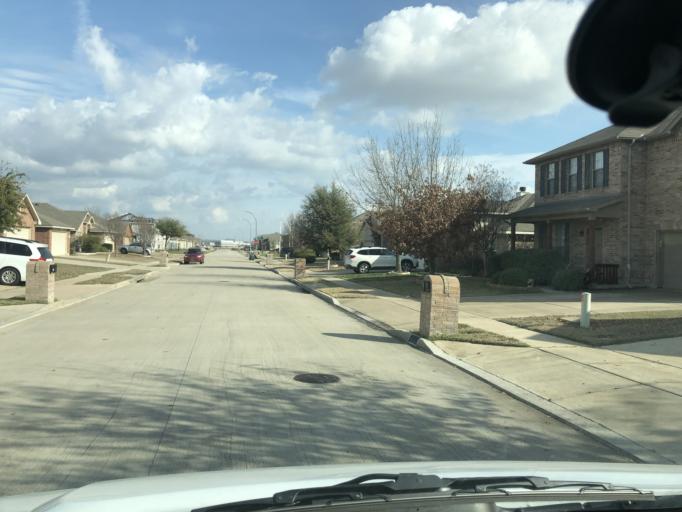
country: US
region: Texas
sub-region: Tarrant County
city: Haslet
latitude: 32.9218
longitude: -97.3670
